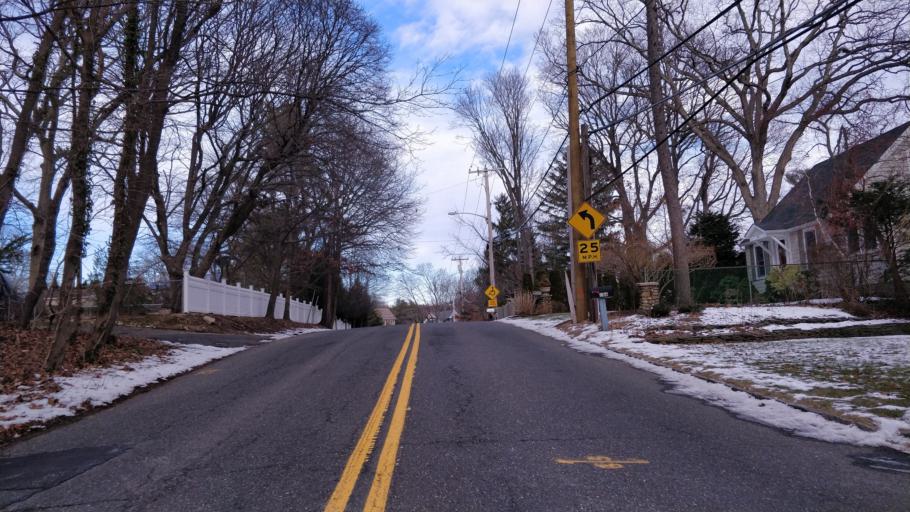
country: US
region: New York
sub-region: Suffolk County
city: Greenlawn
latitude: 40.8758
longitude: -73.3483
